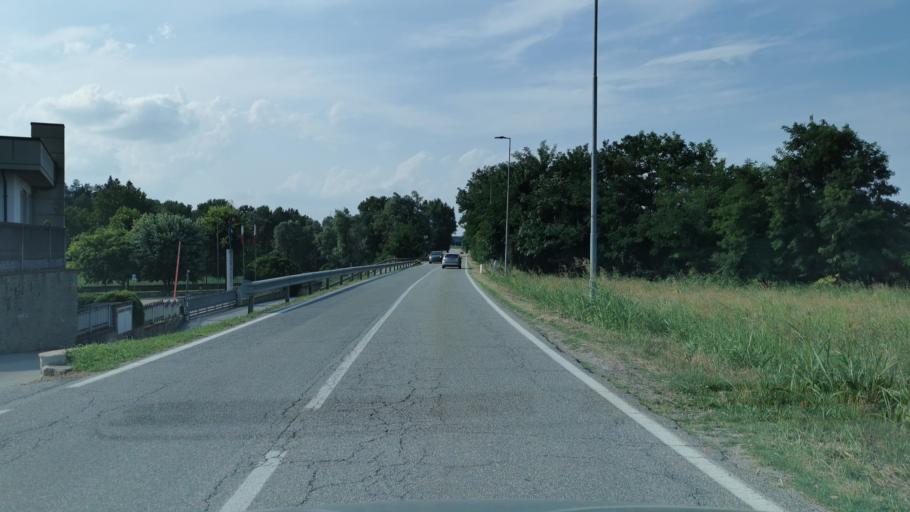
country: IT
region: Piedmont
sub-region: Provincia di Cuneo
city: Cherasco
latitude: 44.6469
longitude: 7.8756
